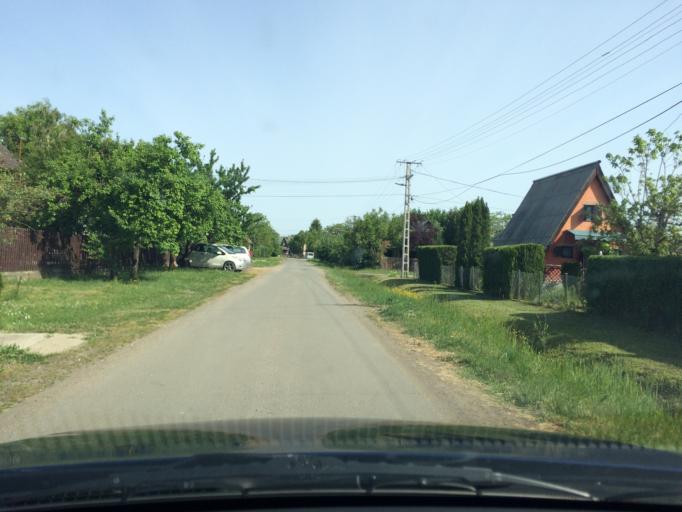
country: HU
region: Szabolcs-Szatmar-Bereg
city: Tiszavasvari
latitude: 47.9530
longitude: 21.3492
